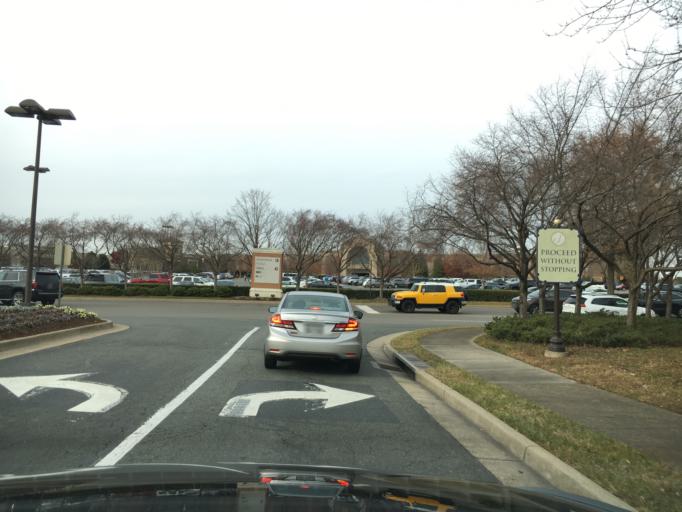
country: US
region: Virginia
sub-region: Henrico County
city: Short Pump
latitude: 37.6536
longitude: -77.6159
